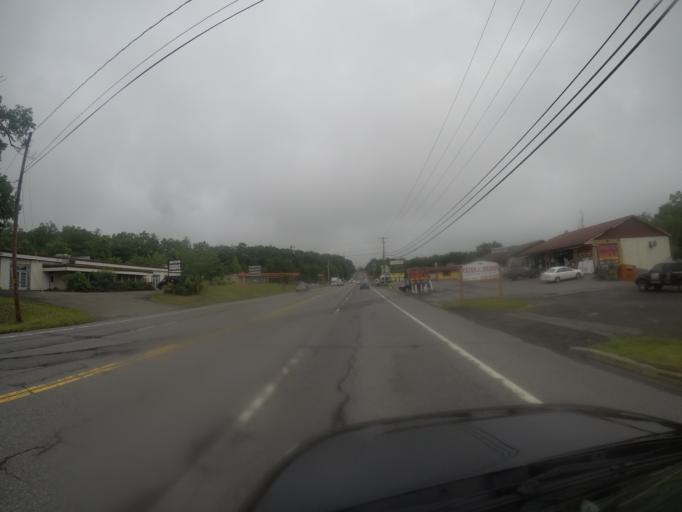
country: US
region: New York
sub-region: Ulster County
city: West Hurley
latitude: 41.9824
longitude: -74.0861
